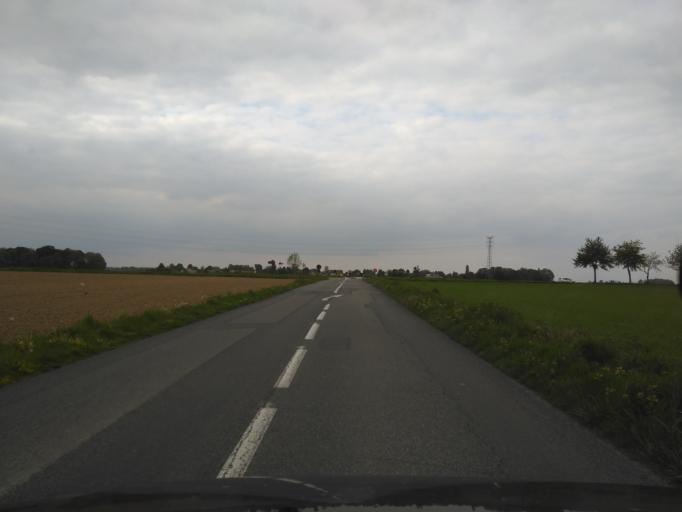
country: FR
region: Ile-de-France
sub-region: Departement de Seine-et-Marne
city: Moisenay
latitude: 48.5756
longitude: 2.7816
